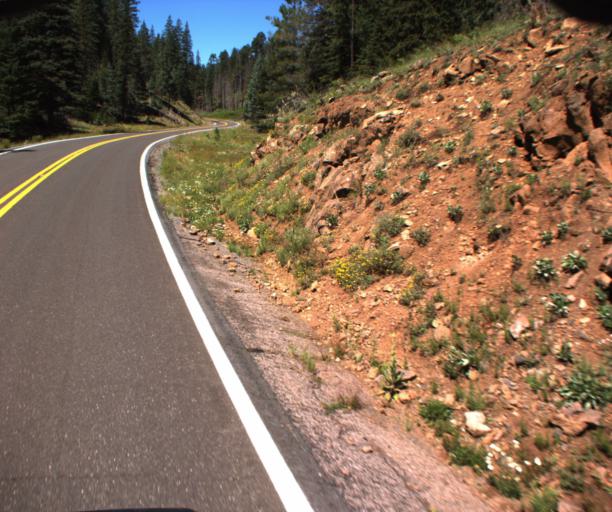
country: US
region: Arizona
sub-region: Apache County
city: Eagar
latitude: 33.6473
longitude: -109.2888
